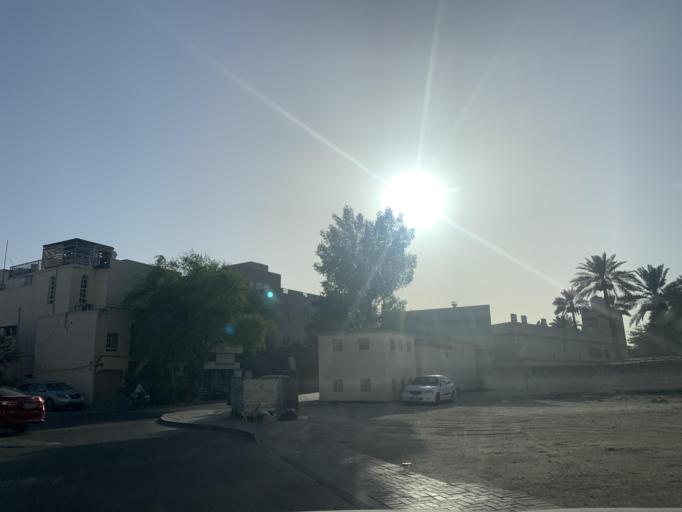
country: BH
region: Manama
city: Jidd Hafs
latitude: 26.2224
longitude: 50.5338
